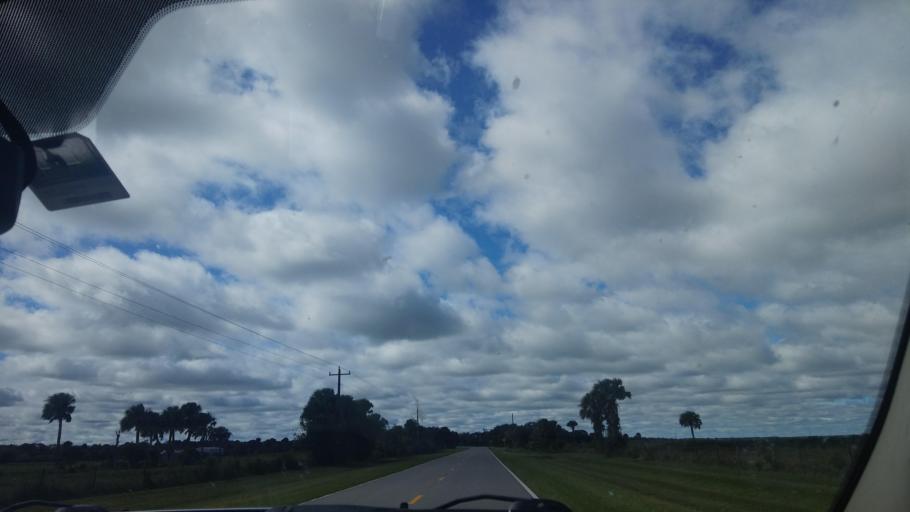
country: US
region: Florida
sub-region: Okeechobee County
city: Okeechobee
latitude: 27.3949
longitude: -80.9083
